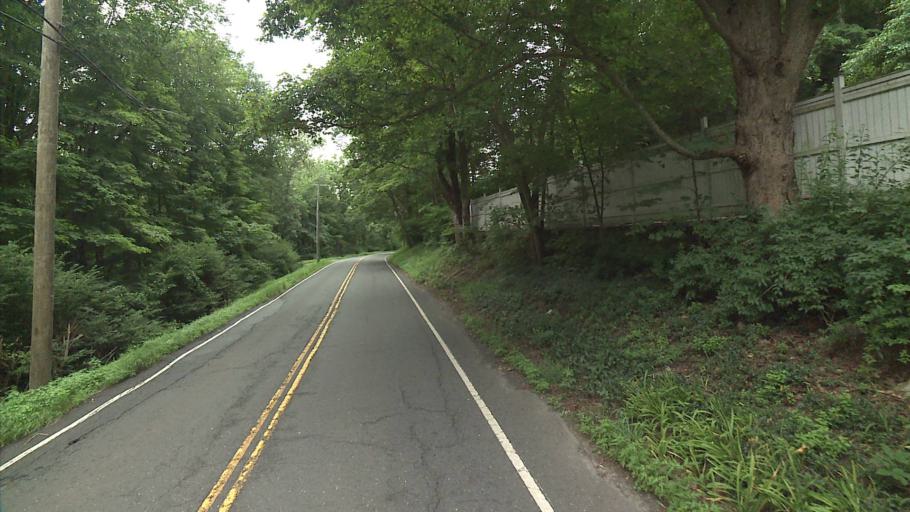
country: US
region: Connecticut
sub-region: Litchfield County
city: New Milford
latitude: 41.5531
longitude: -73.3287
